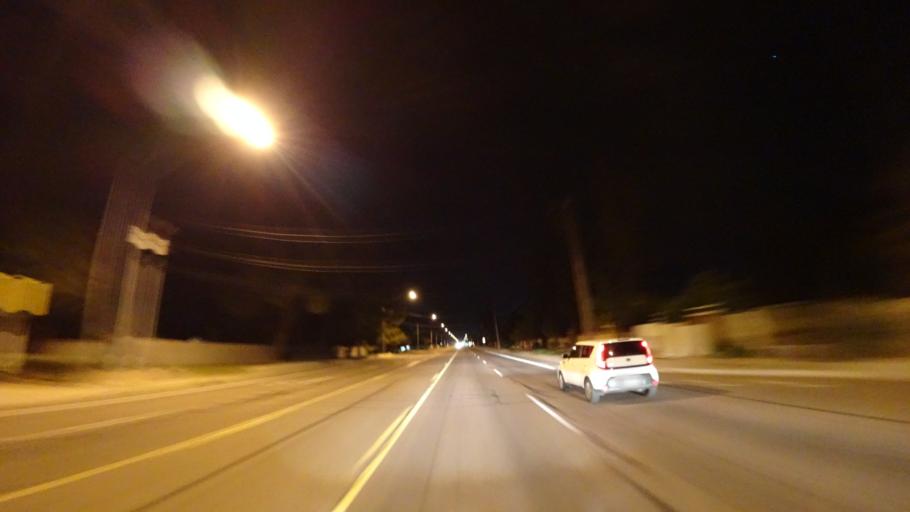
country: US
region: Arizona
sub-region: Maricopa County
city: Gilbert
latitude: 33.3939
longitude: -111.7315
